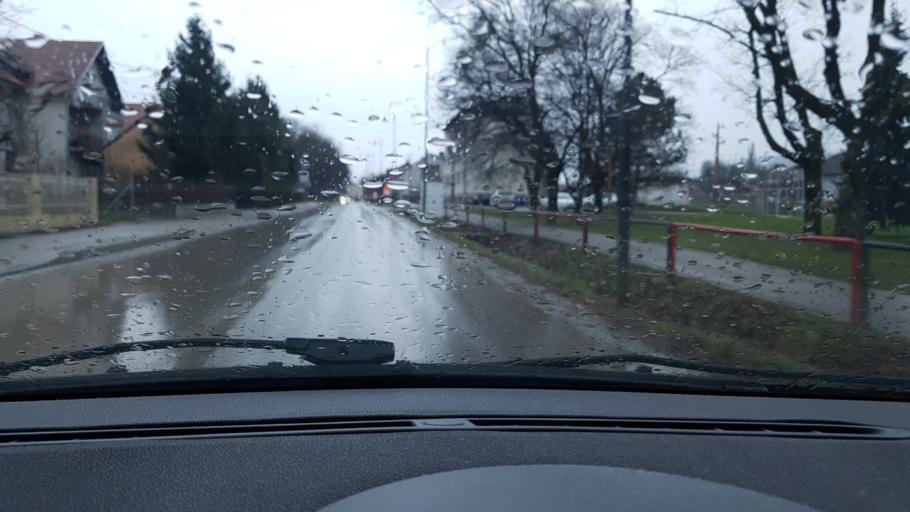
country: HR
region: Krapinsko-Zagorska
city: Oroslavje
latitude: 45.9811
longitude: 15.9632
